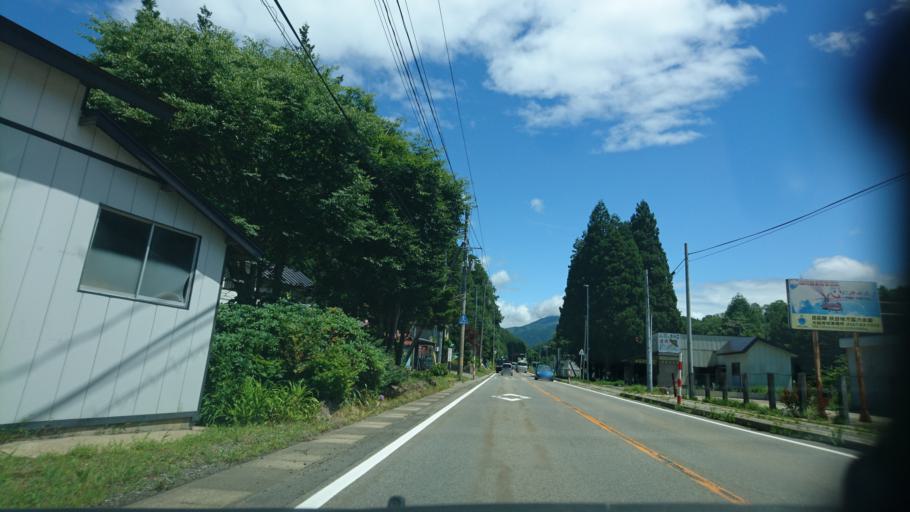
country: JP
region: Akita
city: Kakunodatemachi
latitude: 39.6681
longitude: 140.6912
